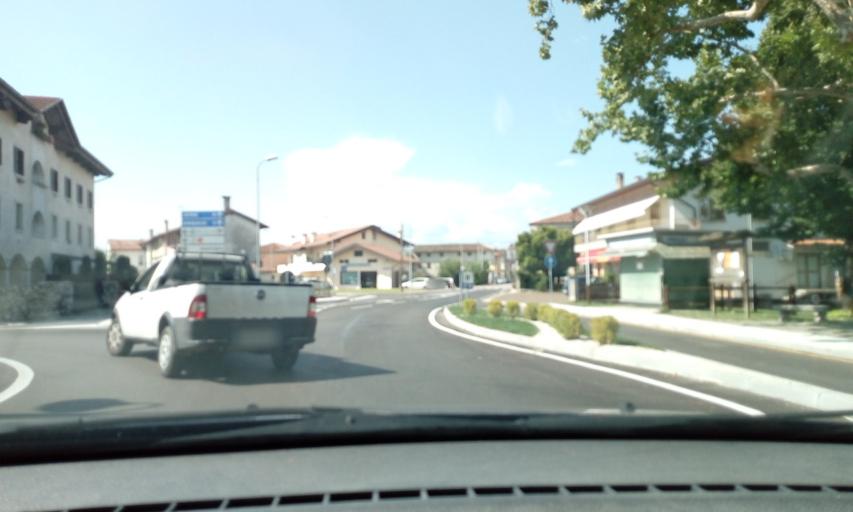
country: IT
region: Friuli Venezia Giulia
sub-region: Provincia di Udine
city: Pradamano
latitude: 46.0327
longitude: 13.3065
